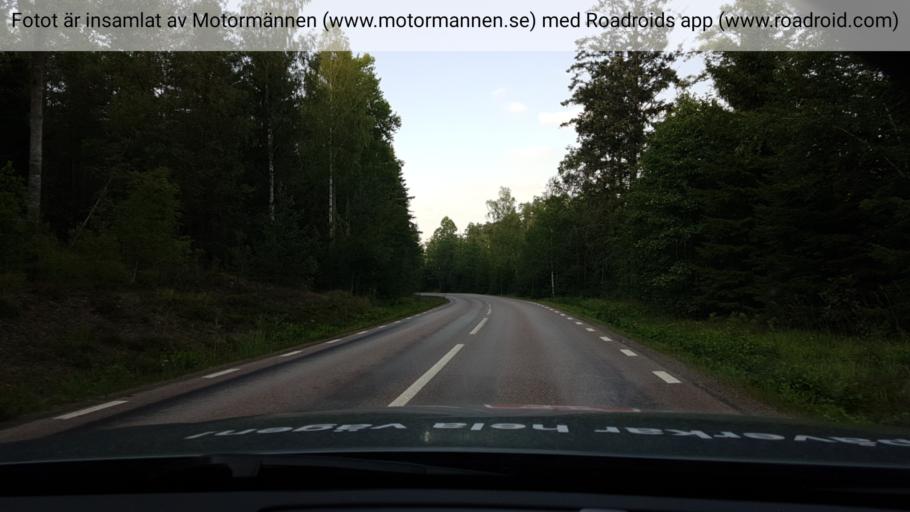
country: SE
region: Soedermanland
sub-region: Strangnas Kommun
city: Mariefred
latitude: 59.2329
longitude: 17.1730
